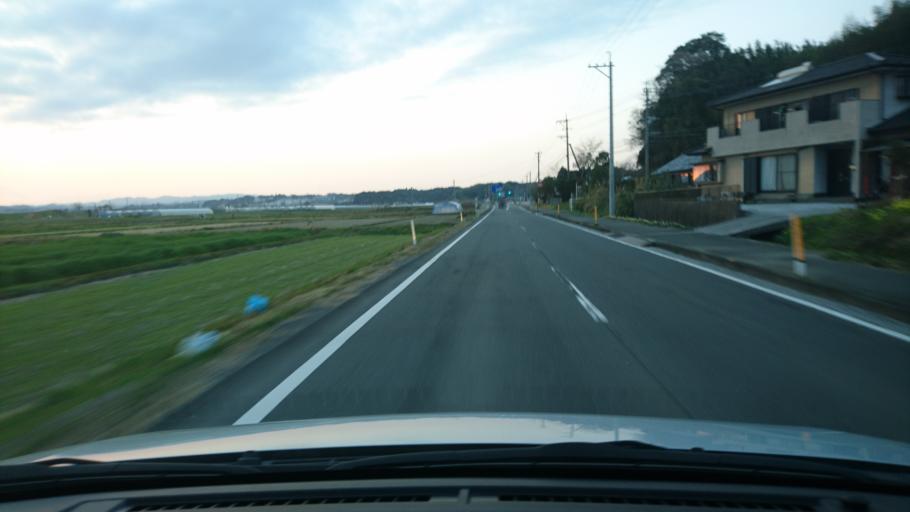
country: JP
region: Miyazaki
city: Miyazaki-shi
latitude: 31.8479
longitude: 131.4235
